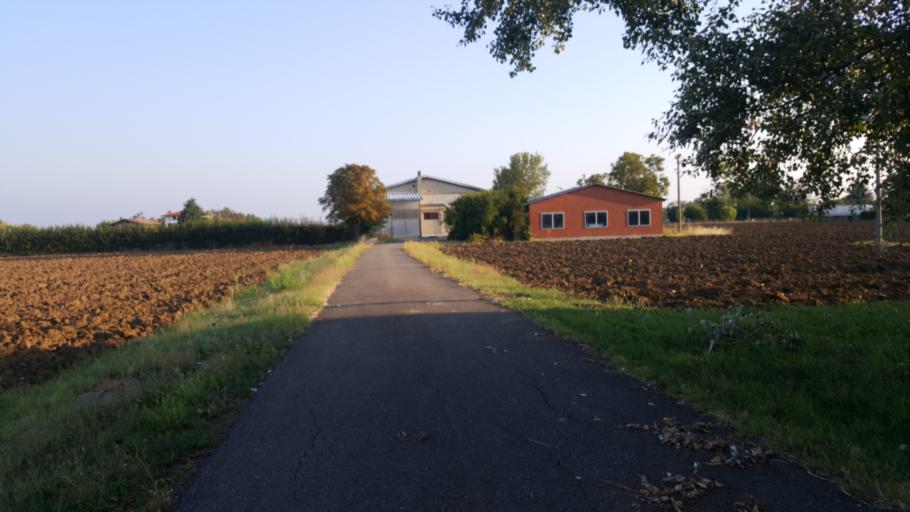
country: IT
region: Lombardy
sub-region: Provincia di Pavia
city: Rivanazzano
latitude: 44.9513
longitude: 9.0127
